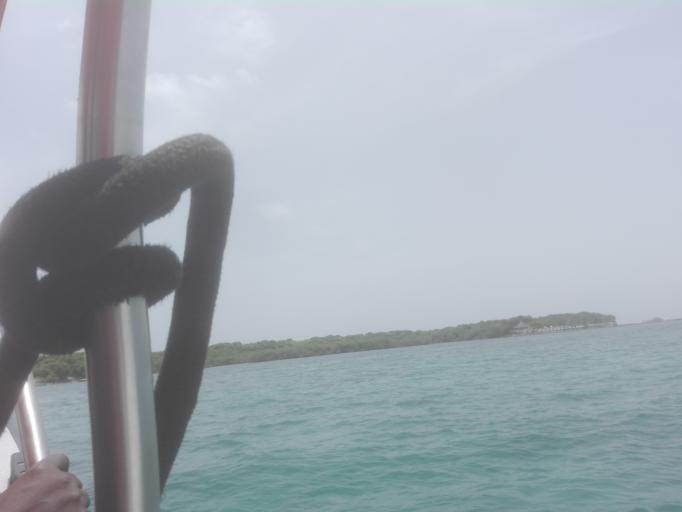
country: CO
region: Bolivar
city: Turbana
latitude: 10.1748
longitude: -75.7296
